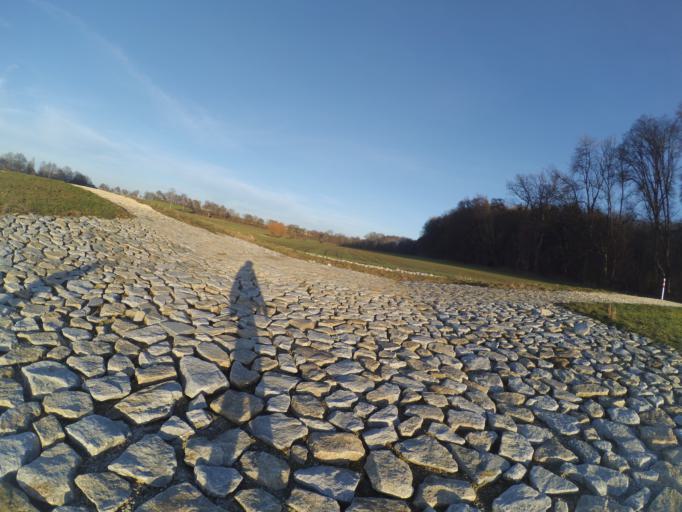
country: DE
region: Bavaria
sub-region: Swabia
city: Guenzburg
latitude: 48.4498
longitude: 10.3011
